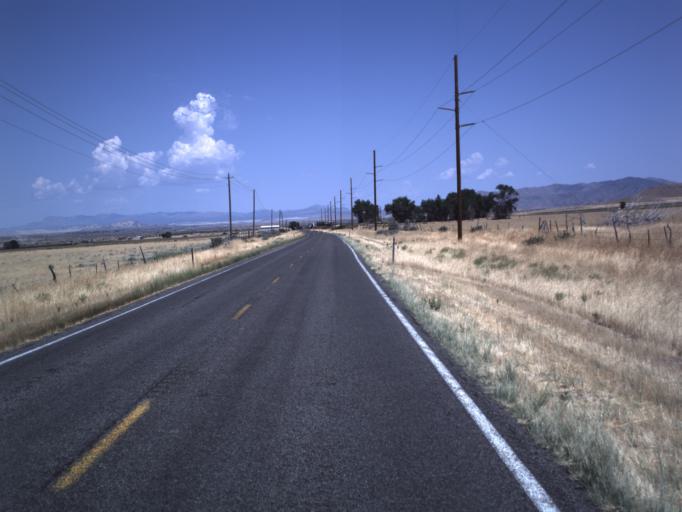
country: US
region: Utah
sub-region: Millard County
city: Delta
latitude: 39.3912
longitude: -112.3356
